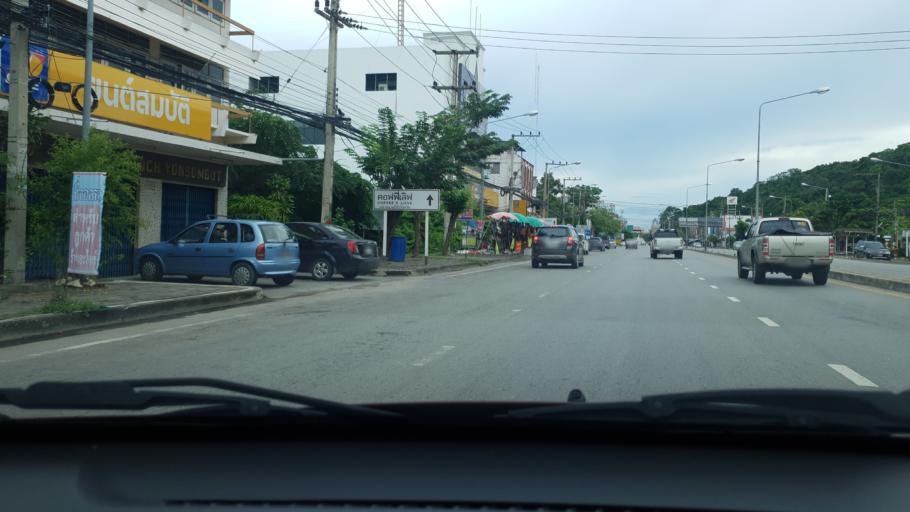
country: TH
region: Phetchaburi
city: Phetchaburi
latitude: 13.1132
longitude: 99.9331
